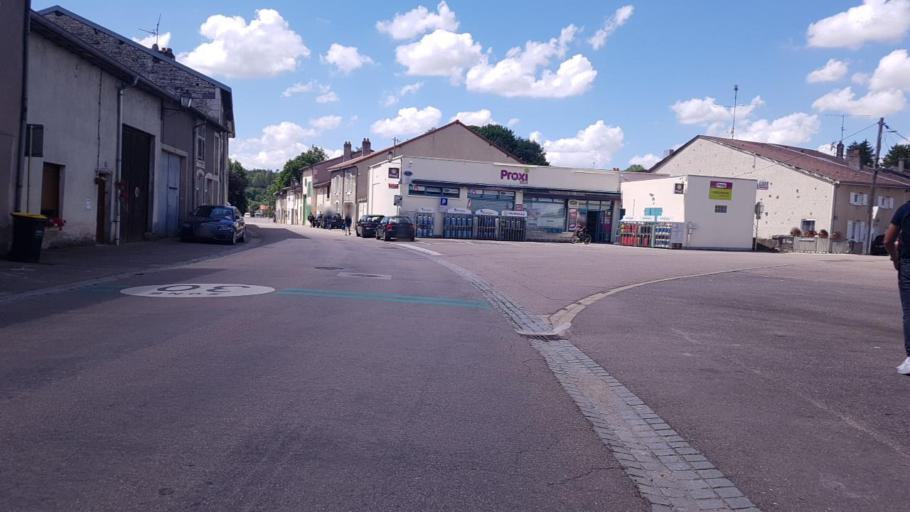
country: FR
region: Lorraine
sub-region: Departement de la Meuse
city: Vacon
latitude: 48.6866
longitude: 5.6174
